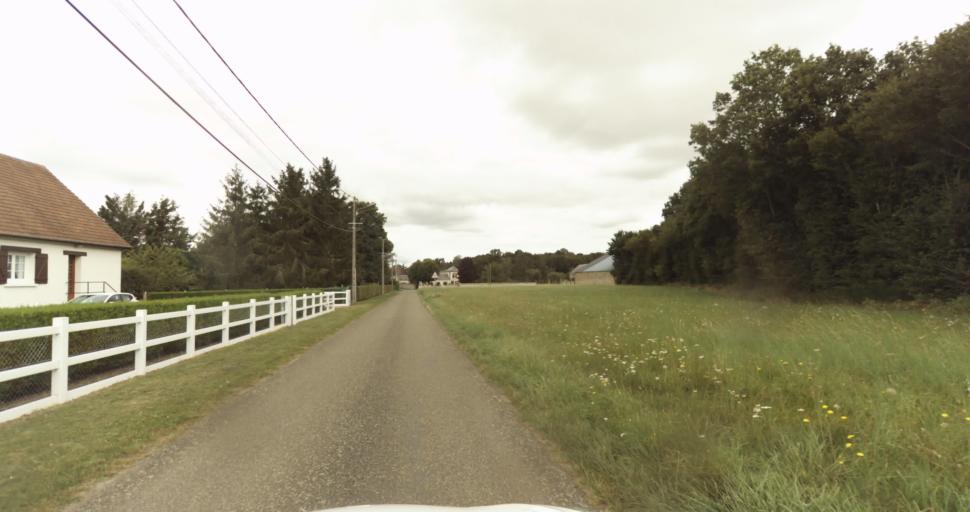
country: FR
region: Haute-Normandie
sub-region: Departement de l'Eure
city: La Madeleine-de-Nonancourt
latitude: 48.8363
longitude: 1.2165
